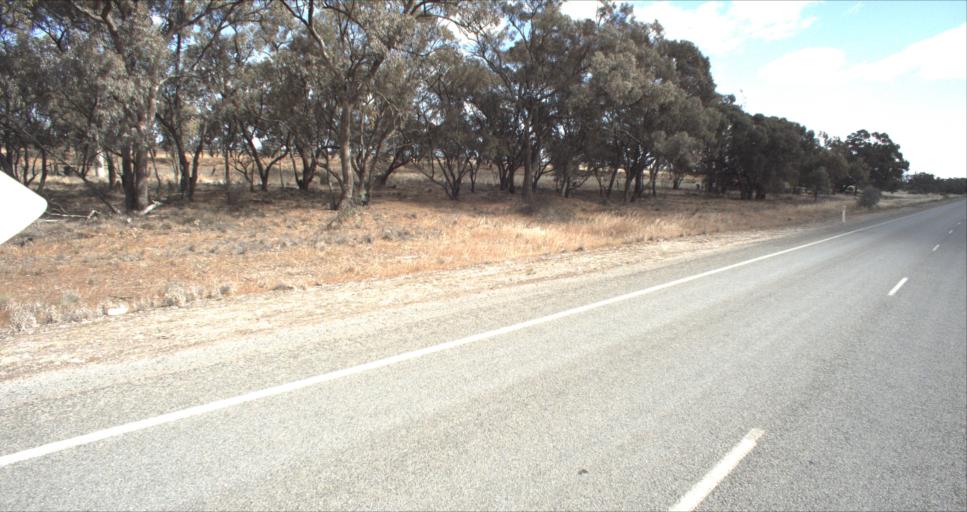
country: AU
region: New South Wales
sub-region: Murrumbidgee Shire
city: Darlington Point
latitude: -34.5726
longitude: 146.1669
